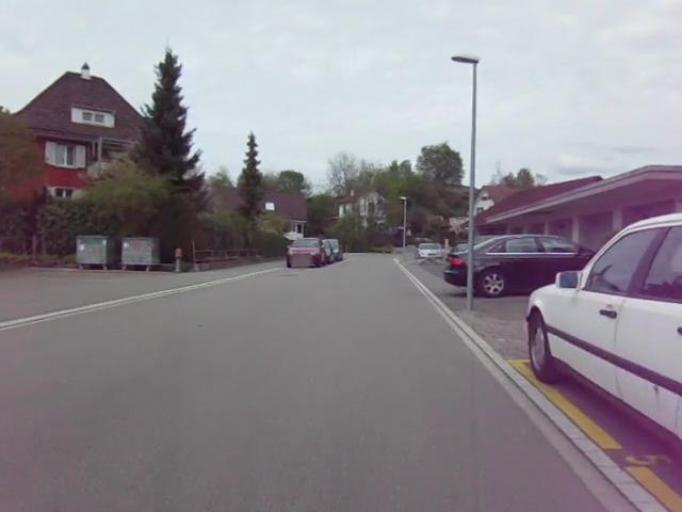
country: CH
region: Zurich
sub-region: Bezirk Hinwil
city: Rueti / Westlicher Dorfteil
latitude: 47.2545
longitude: 8.8438
